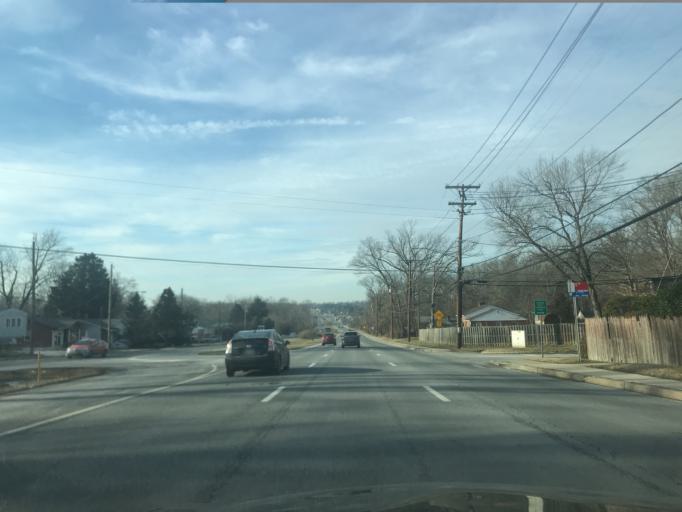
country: US
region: Maryland
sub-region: Montgomery County
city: Aspen Hill
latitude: 39.0736
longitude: -77.0659
